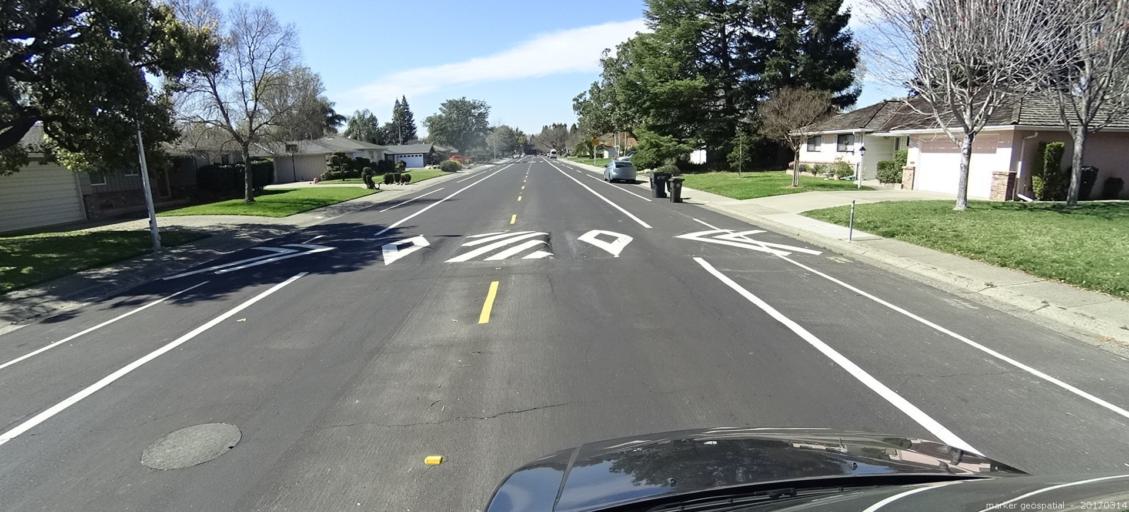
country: US
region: California
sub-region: Yolo County
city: West Sacramento
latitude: 38.5217
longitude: -121.5149
